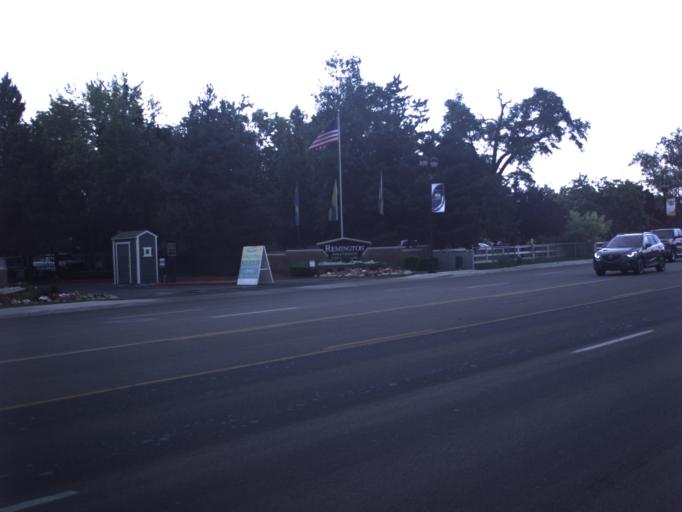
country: US
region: Utah
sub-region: Salt Lake County
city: Midvale
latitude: 40.6170
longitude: -111.8905
